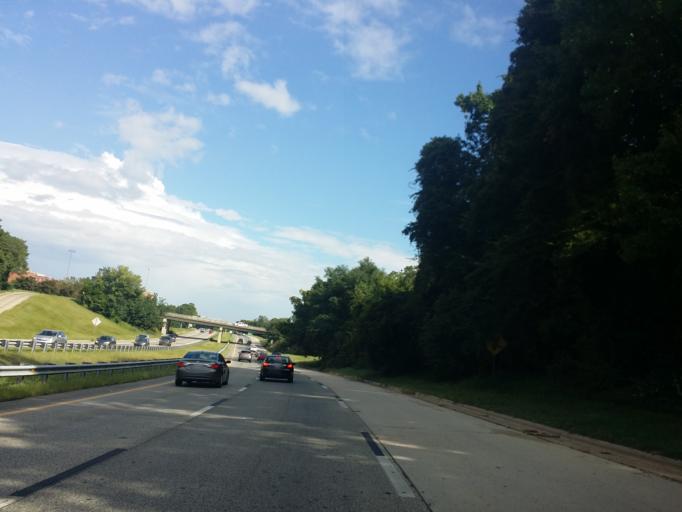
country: US
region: North Carolina
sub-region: Durham County
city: Durham
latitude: 35.9938
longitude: -78.9111
